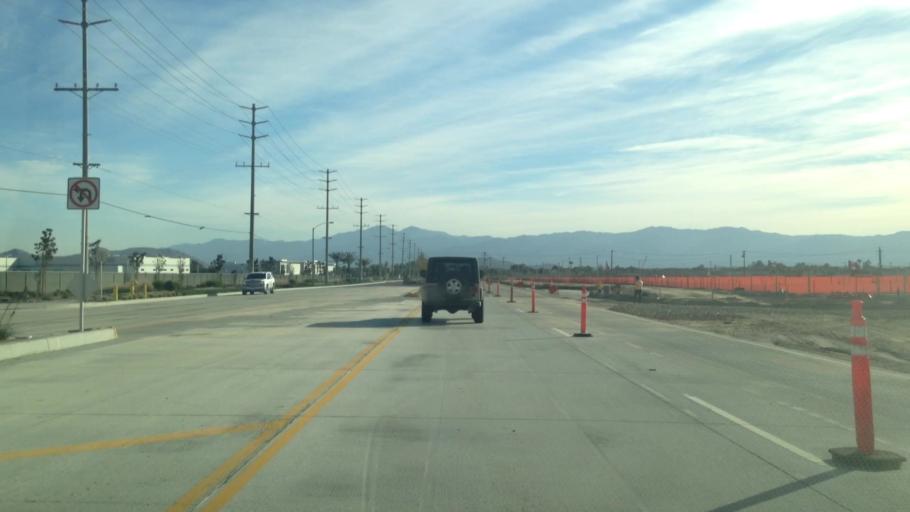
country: US
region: California
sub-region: Riverside County
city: Mira Loma
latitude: 33.9937
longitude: -117.5585
